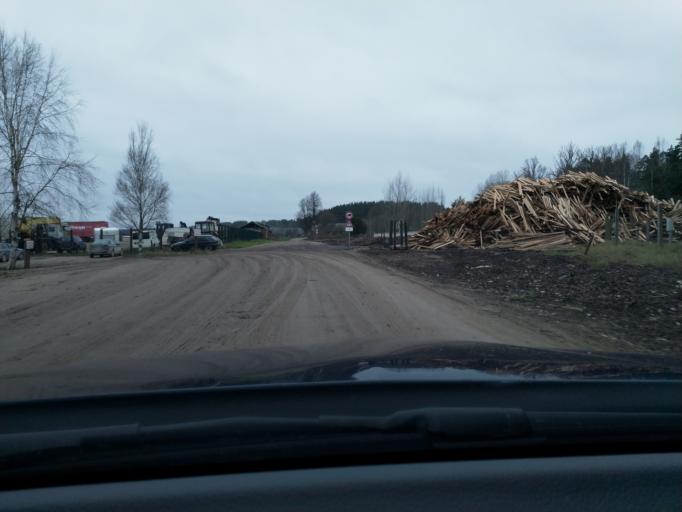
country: LV
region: Ventspils Rajons
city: Piltene
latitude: 57.1291
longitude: 21.8013
